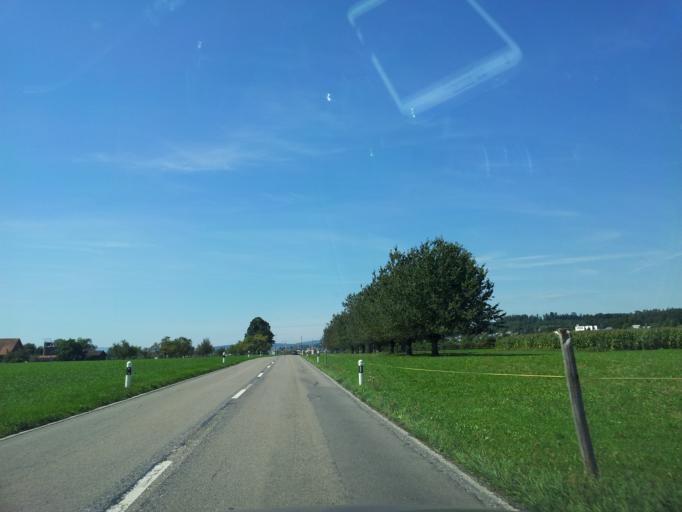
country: CH
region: Schwyz
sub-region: Bezirk March
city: Lachen
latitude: 47.2203
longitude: 8.8706
